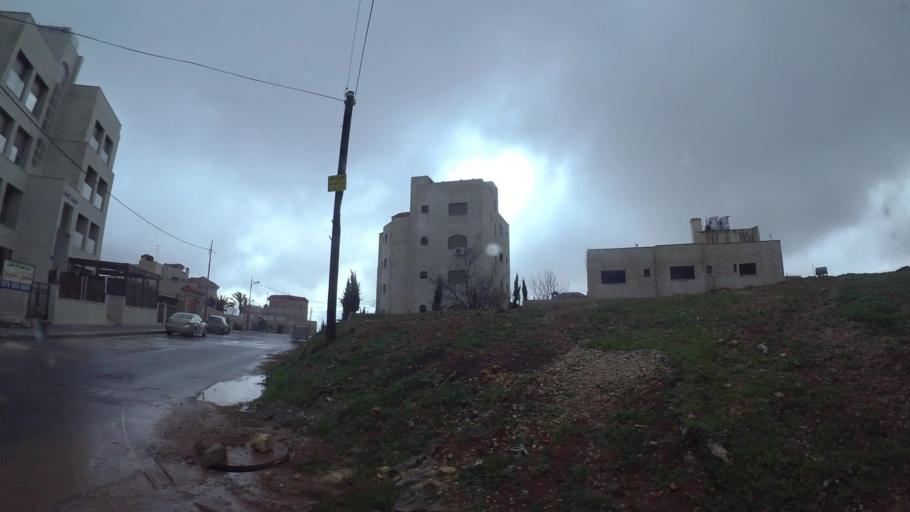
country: JO
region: Amman
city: Al Jubayhah
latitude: 32.0342
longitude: 35.8579
